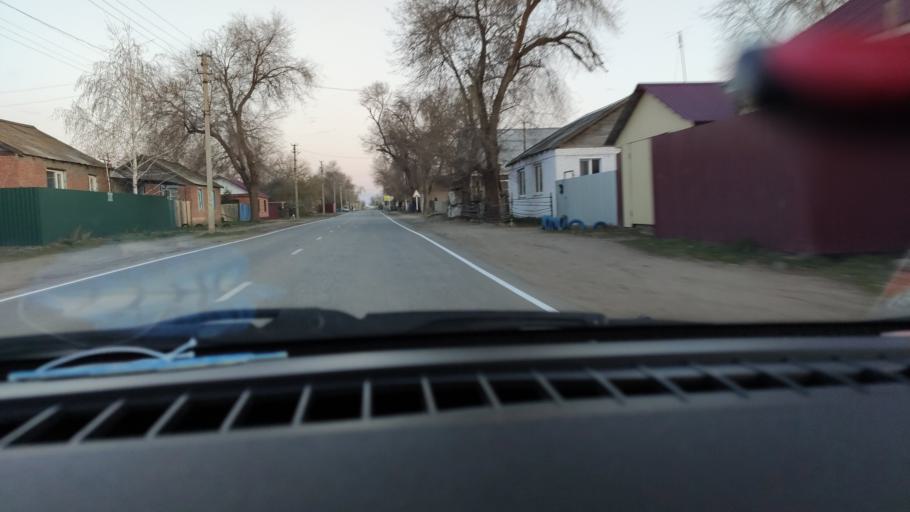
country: RU
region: Saratov
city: Privolzhskiy
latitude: 51.1844
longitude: 45.9181
